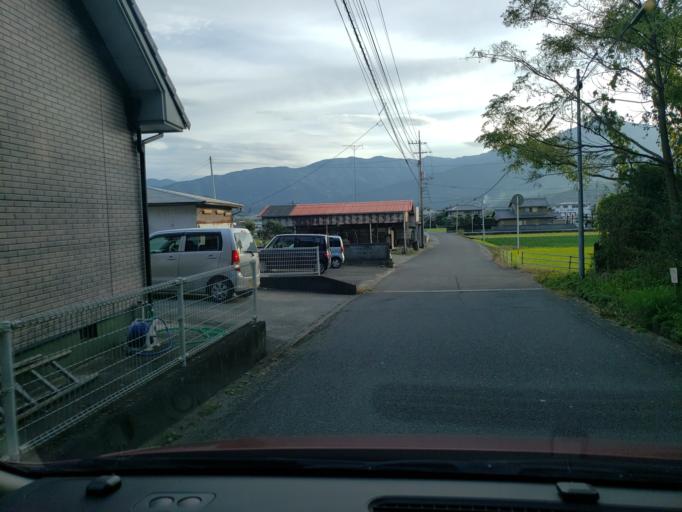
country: JP
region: Tokushima
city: Wakimachi
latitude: 34.0768
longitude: 134.2279
